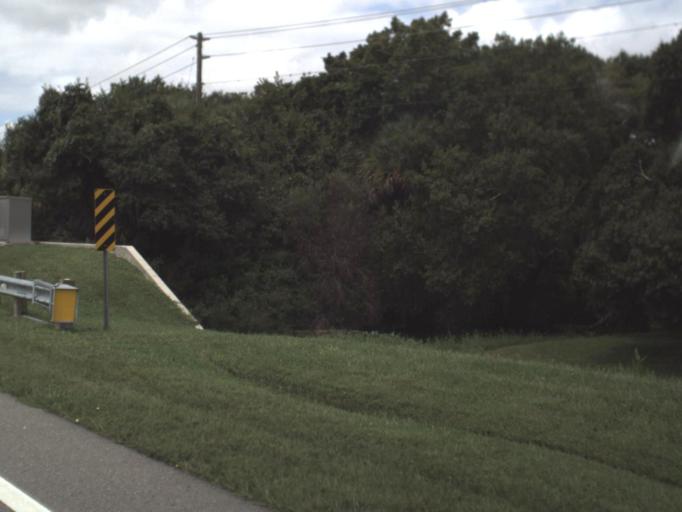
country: US
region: Florida
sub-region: Sarasota County
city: The Meadows
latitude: 27.3886
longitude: -82.4592
